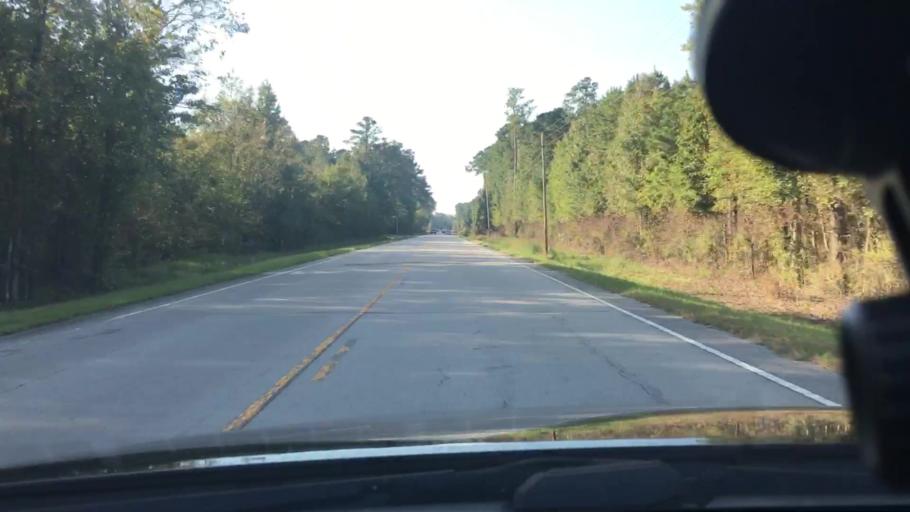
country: US
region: North Carolina
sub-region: Craven County
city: Vanceboro
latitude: 35.4101
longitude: -77.2460
